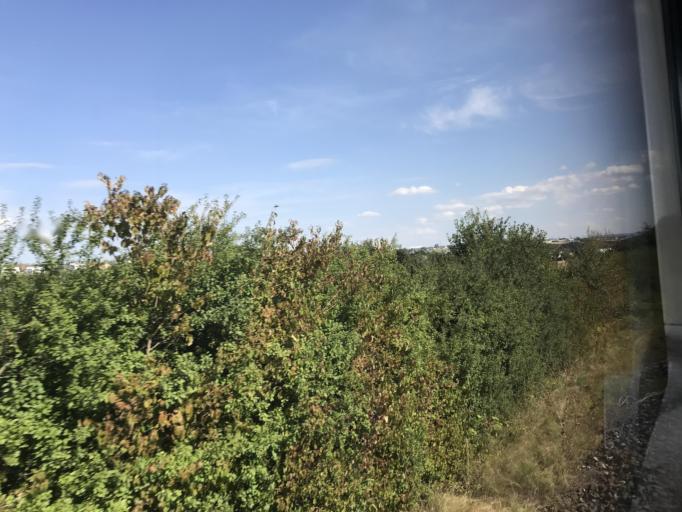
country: DE
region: Rheinland-Pfalz
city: Guckingen
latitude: 50.4139
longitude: 8.0167
